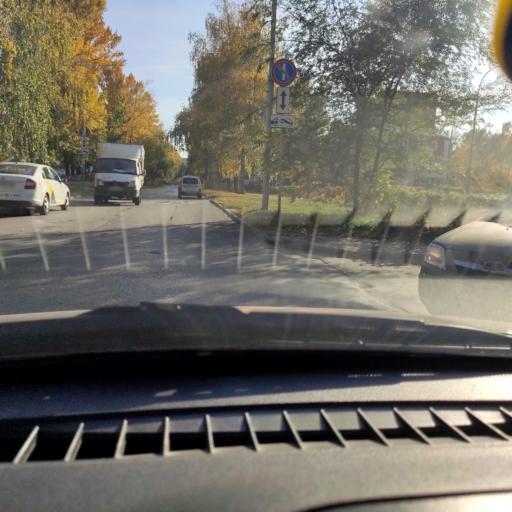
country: RU
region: Samara
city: Tol'yatti
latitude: 53.5105
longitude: 49.2840
